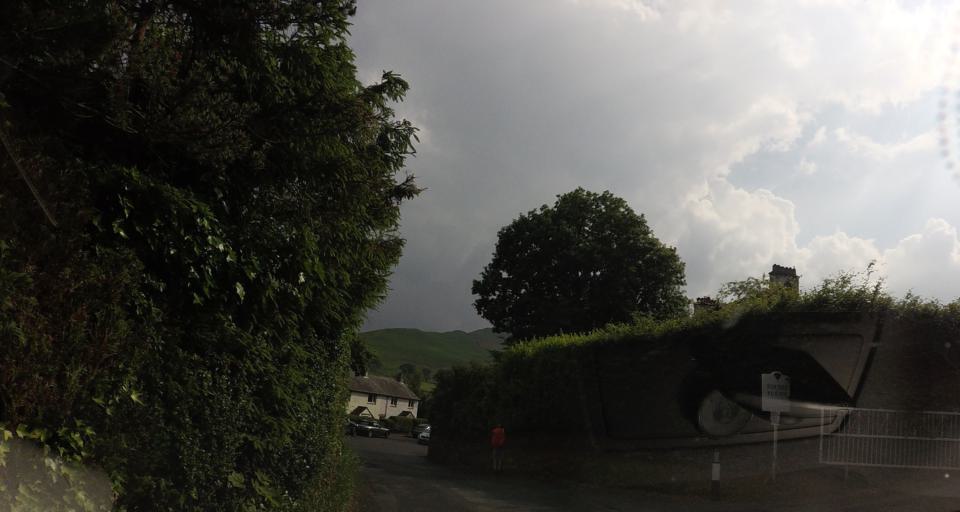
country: GB
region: England
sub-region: Cumbria
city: Keswick
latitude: 54.6040
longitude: -3.1891
